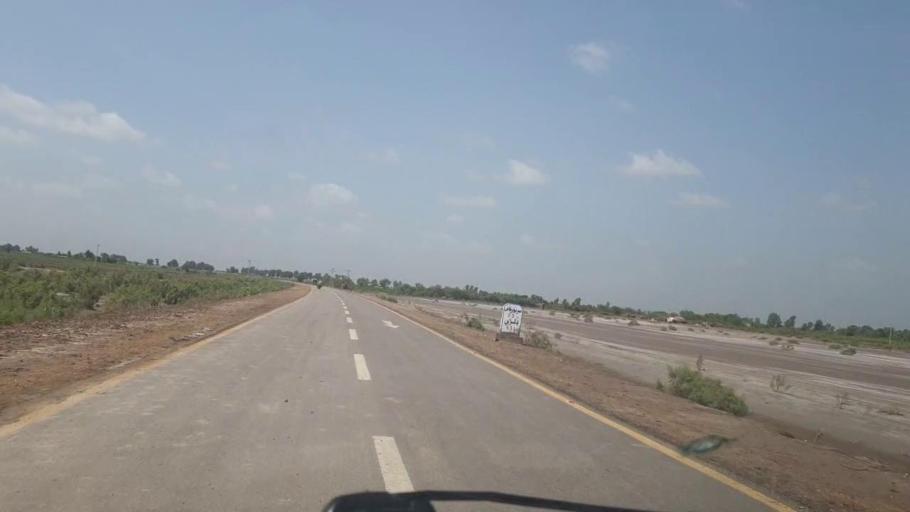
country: PK
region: Sindh
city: Berani
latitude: 25.7116
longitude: 68.9435
